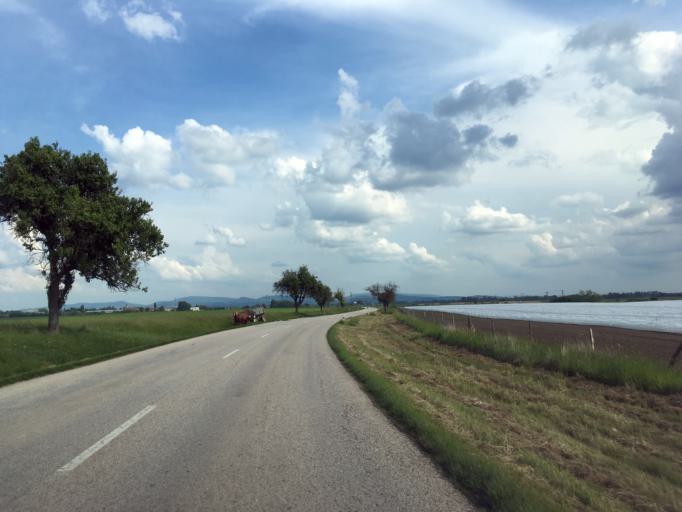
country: HU
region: Komarom-Esztergom
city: Almasfuzito
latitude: 47.7953
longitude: 18.2512
